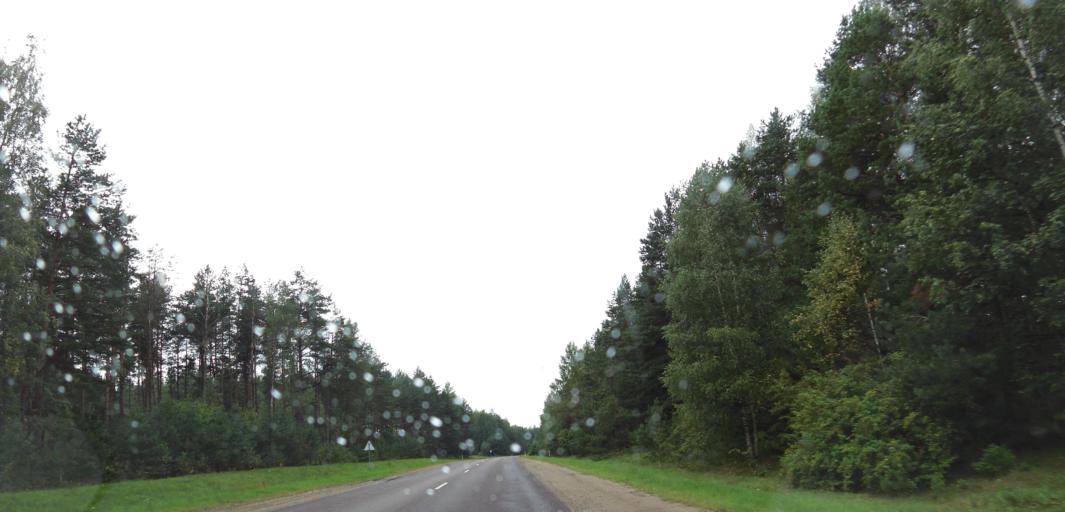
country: LT
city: Moletai
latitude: 55.2189
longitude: 25.3863
